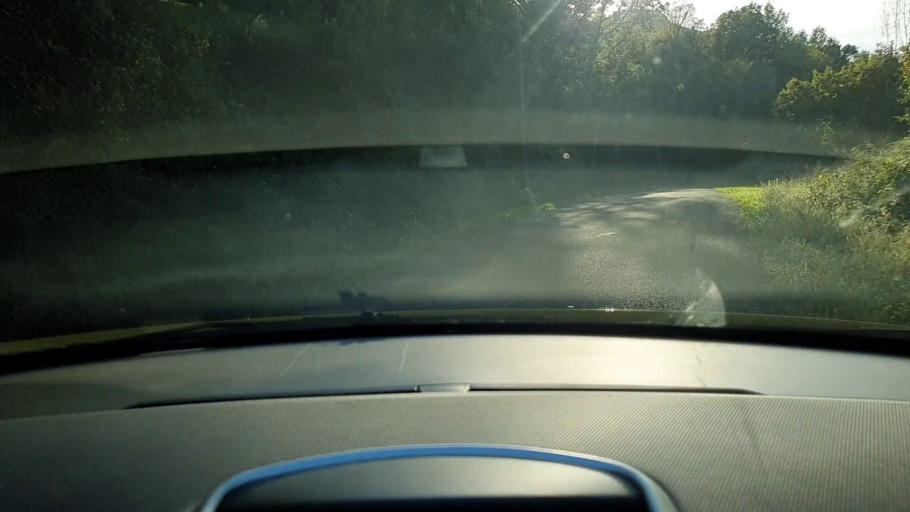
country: FR
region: Languedoc-Roussillon
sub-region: Departement du Gard
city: Sumene
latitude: 43.9834
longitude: 3.7419
